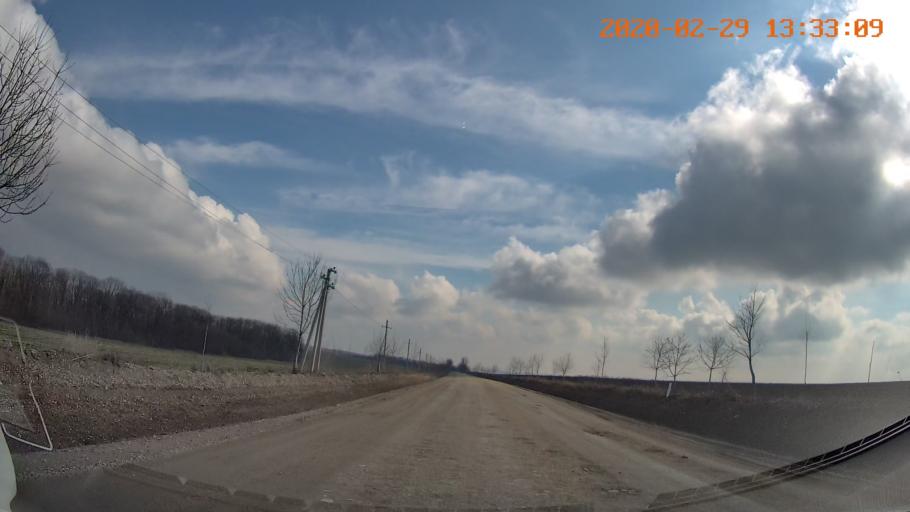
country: MD
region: Telenesti
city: Camenca
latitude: 47.8752
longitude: 28.6144
